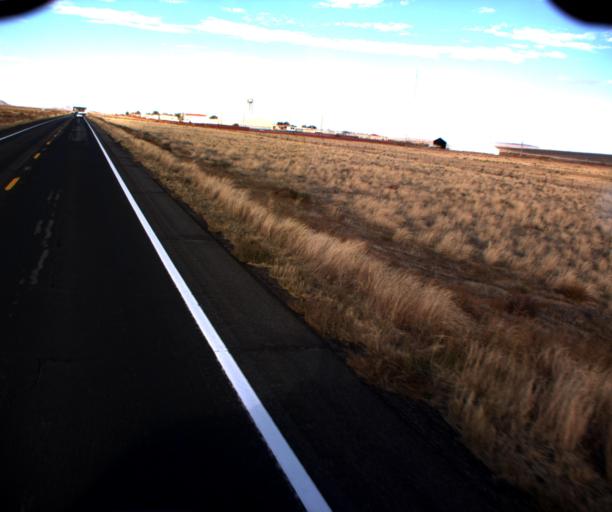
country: US
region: Arizona
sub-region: Apache County
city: Lukachukai
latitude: 36.9606
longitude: -109.3738
